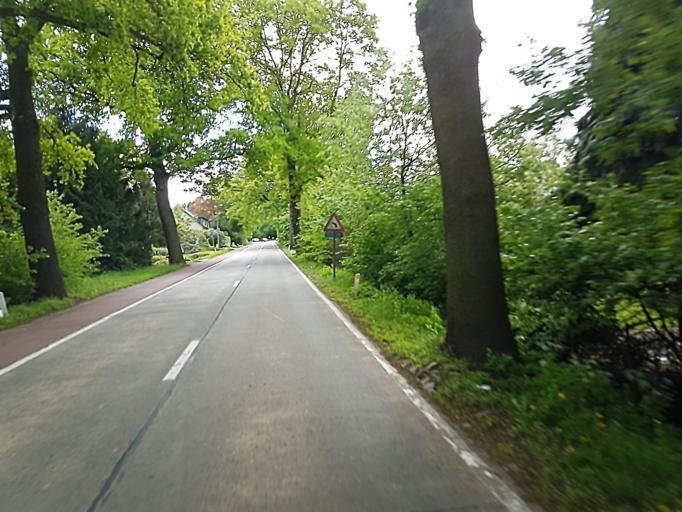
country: BE
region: Flanders
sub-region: Provincie Vlaams-Brabant
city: Diest
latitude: 51.0006
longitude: 5.0304
